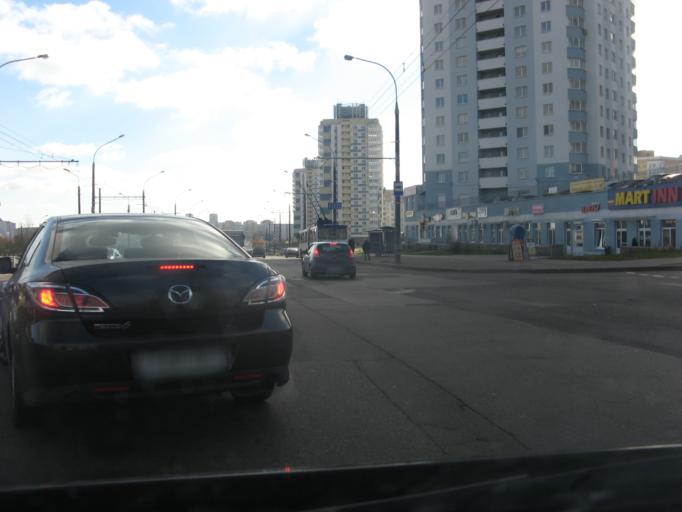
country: BY
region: Minsk
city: Novoye Medvezhino
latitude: 53.8812
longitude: 27.4536
